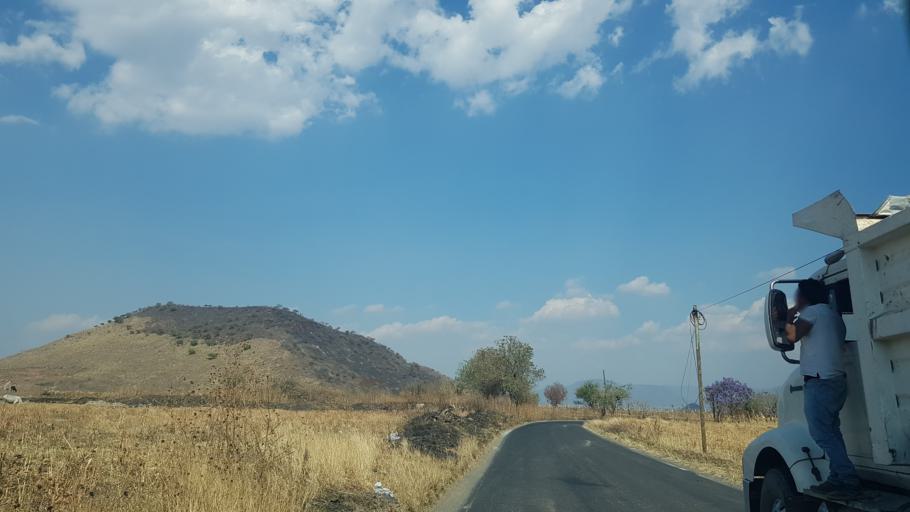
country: MX
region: Puebla
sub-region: Tianguismanalco
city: San Martin Tlapala
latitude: 18.9236
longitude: -98.4846
